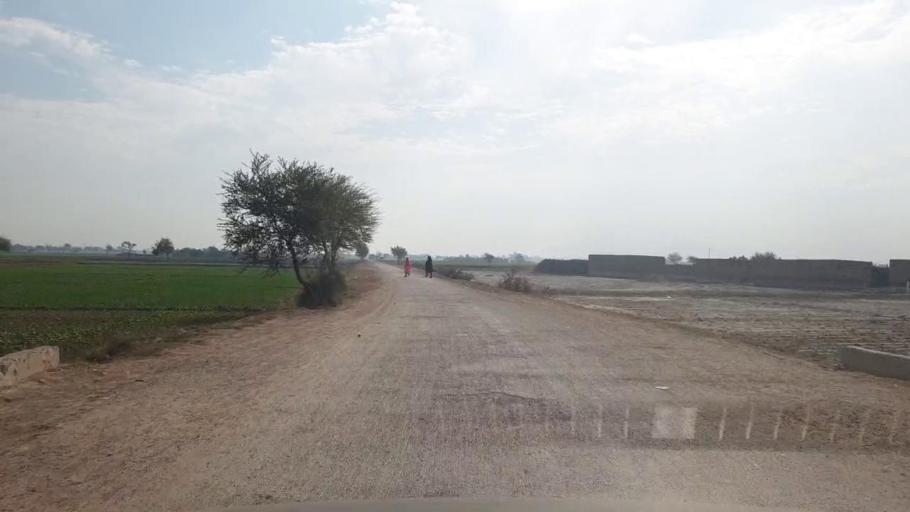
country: PK
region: Sindh
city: Hala
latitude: 26.0001
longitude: 68.4067
